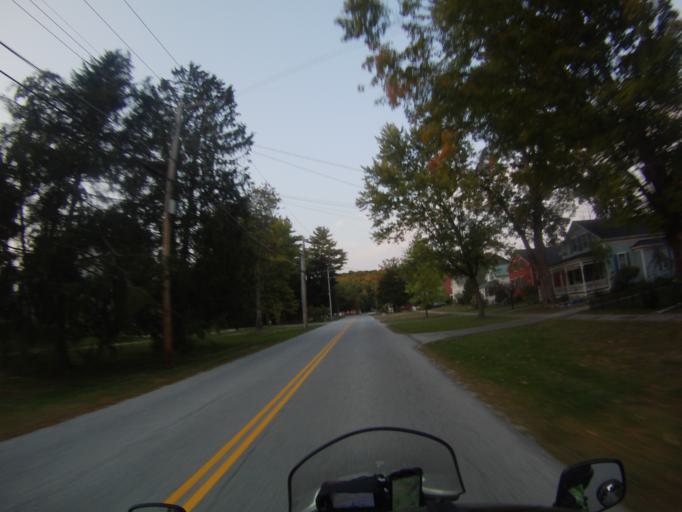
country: US
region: Vermont
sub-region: Rutland County
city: Brandon
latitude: 43.7986
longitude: -73.0939
